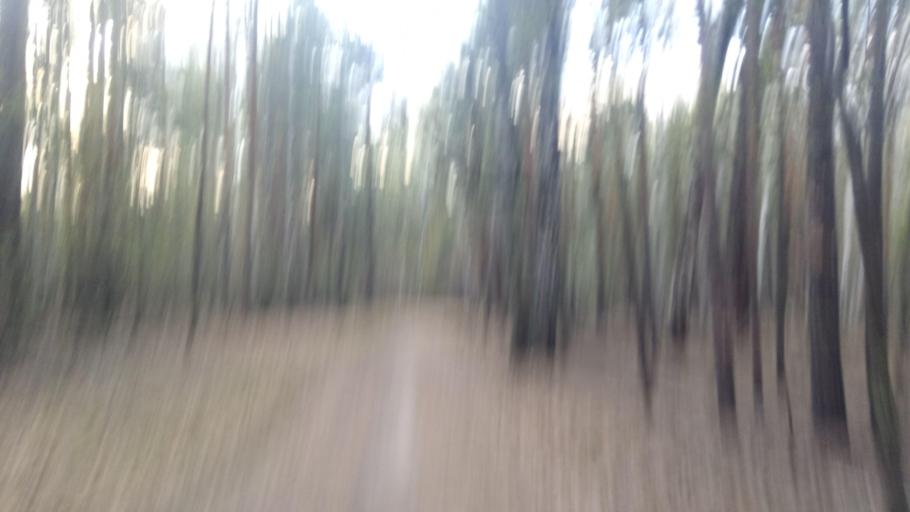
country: RU
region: Chelyabinsk
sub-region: Gorod Chelyabinsk
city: Chelyabinsk
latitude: 55.1483
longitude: 61.3374
